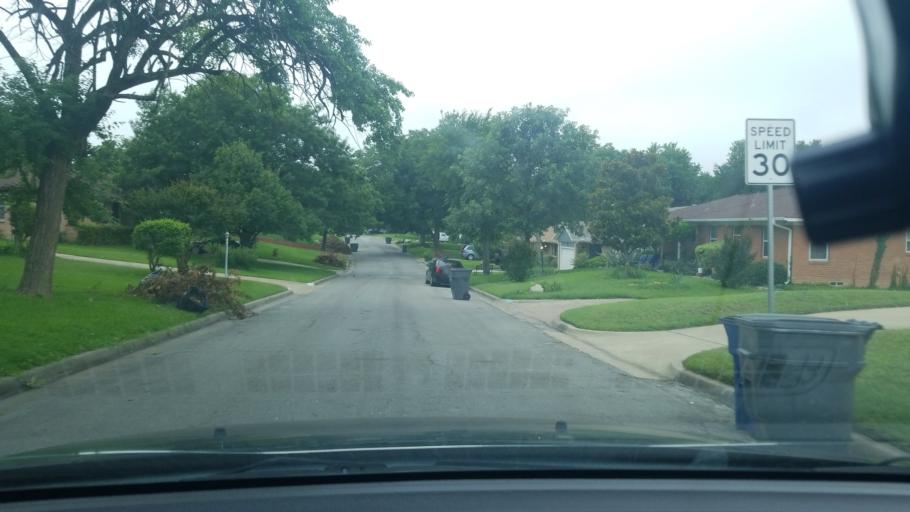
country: US
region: Texas
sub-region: Dallas County
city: Balch Springs
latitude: 32.7588
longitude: -96.6924
